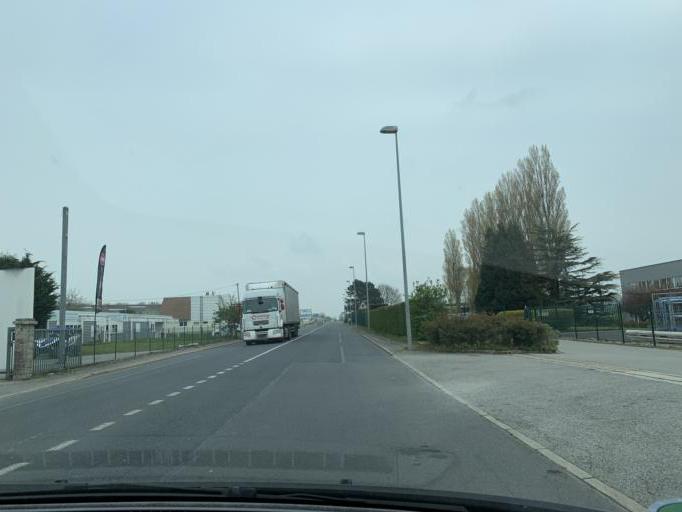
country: FR
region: Haute-Normandie
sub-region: Departement de la Seine-Maritime
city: Dieppe
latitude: 49.9228
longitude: 1.1134
